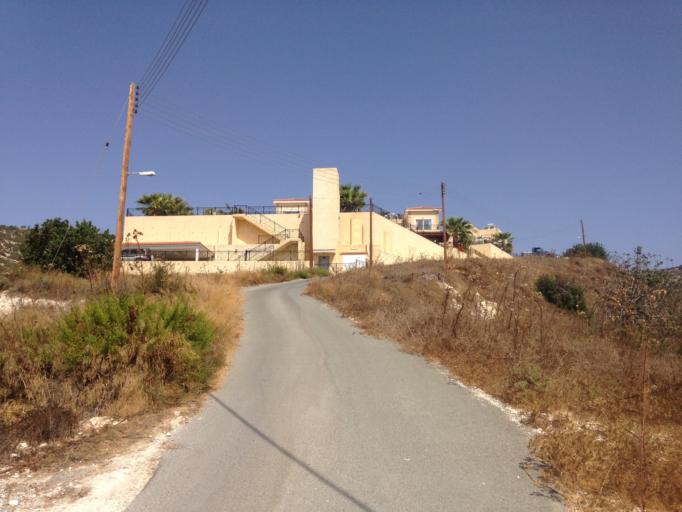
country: CY
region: Pafos
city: Pegeia
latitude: 34.8907
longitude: 32.3873
